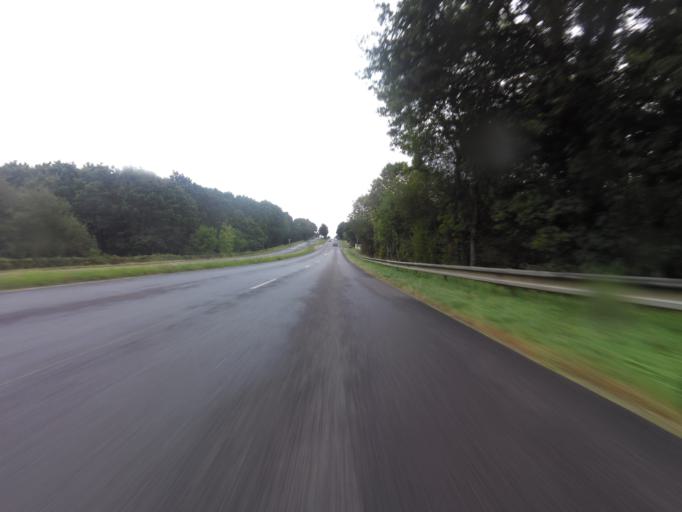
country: FR
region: Brittany
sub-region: Departement du Morbihan
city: Saint-Nolff
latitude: 47.6892
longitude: -2.6775
